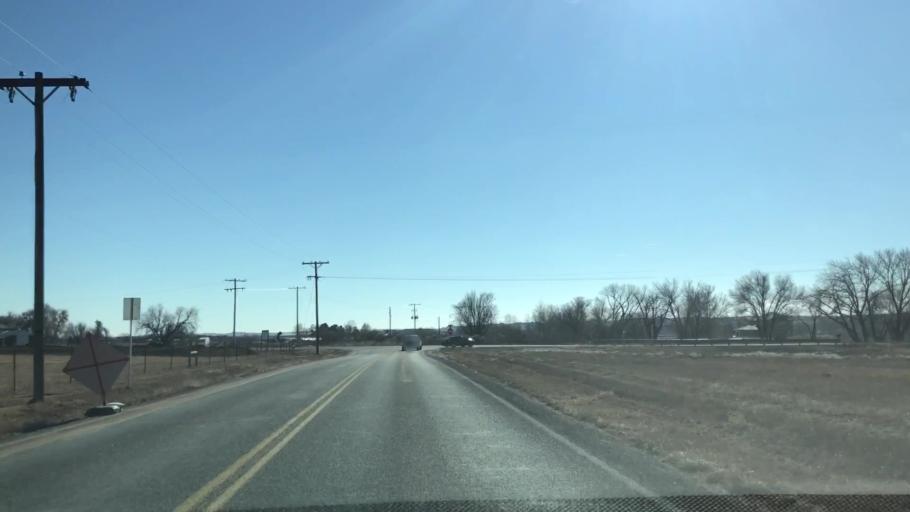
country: US
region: Colorado
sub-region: Weld County
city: Windsor
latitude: 40.4874
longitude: -104.9408
